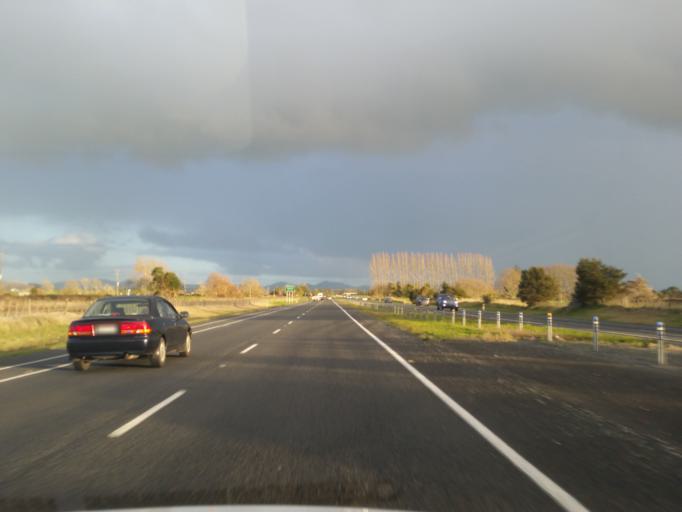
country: NZ
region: Waikato
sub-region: Waikato District
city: Te Kauwhata
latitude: -37.4744
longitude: 175.1594
